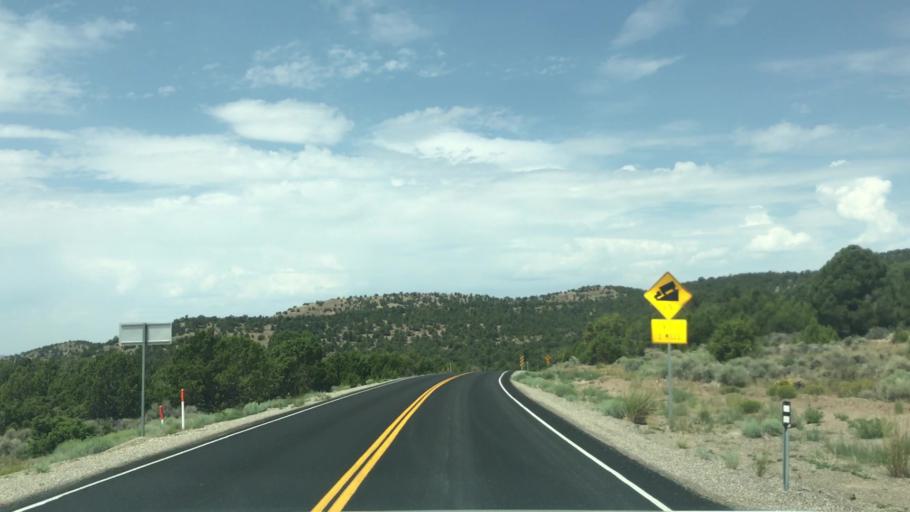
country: US
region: Nevada
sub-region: Eureka County
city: Eureka
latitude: 39.3975
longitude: -115.4689
